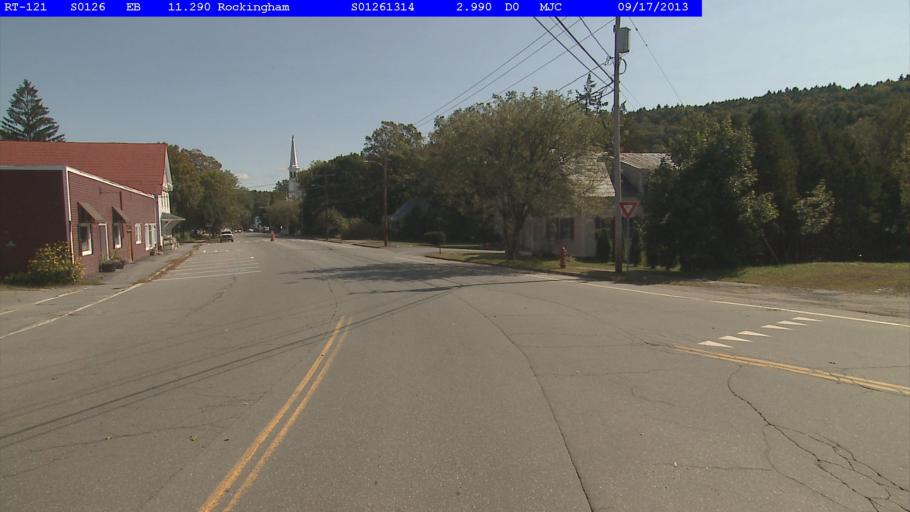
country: US
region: Vermont
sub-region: Windham County
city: Rockingham
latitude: 43.1383
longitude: -72.5094
